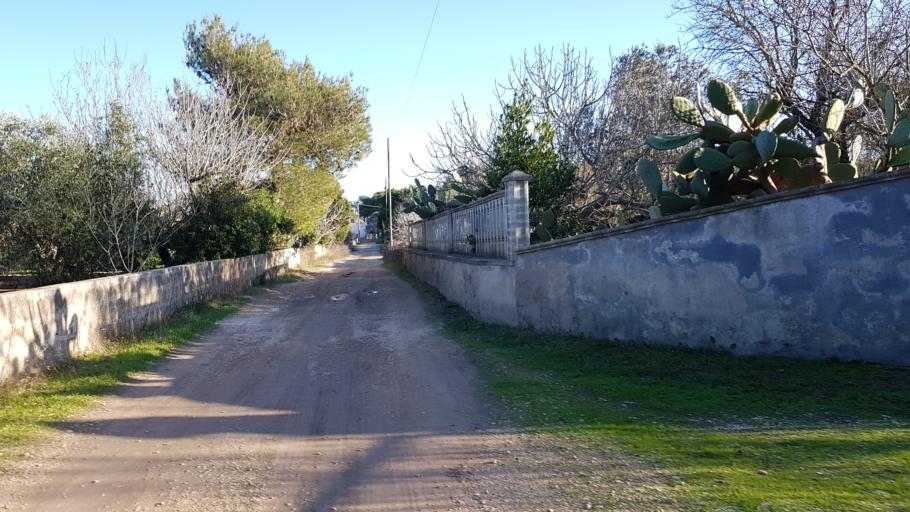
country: IT
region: Apulia
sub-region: Provincia di Lecce
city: Nardo
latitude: 40.1576
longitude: 17.9730
